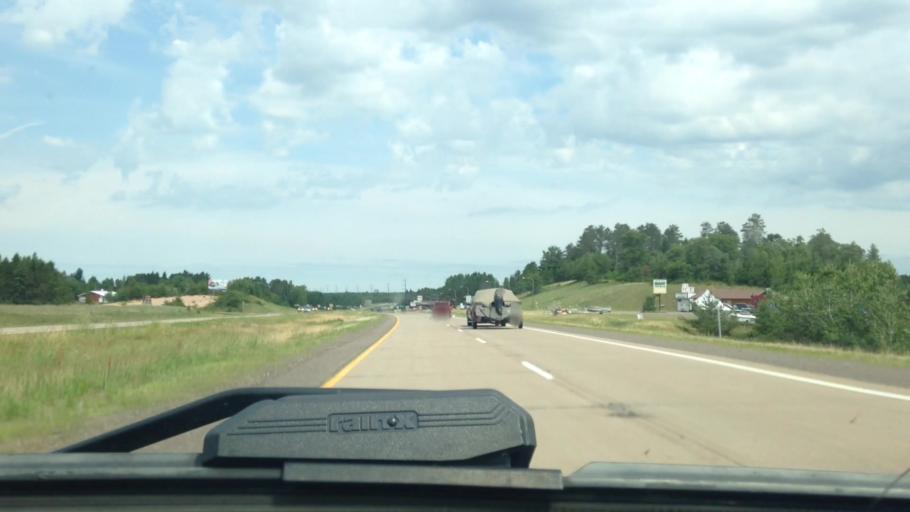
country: US
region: Wisconsin
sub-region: Douglas County
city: Lake Nebagamon
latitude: 46.2387
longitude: -91.8005
